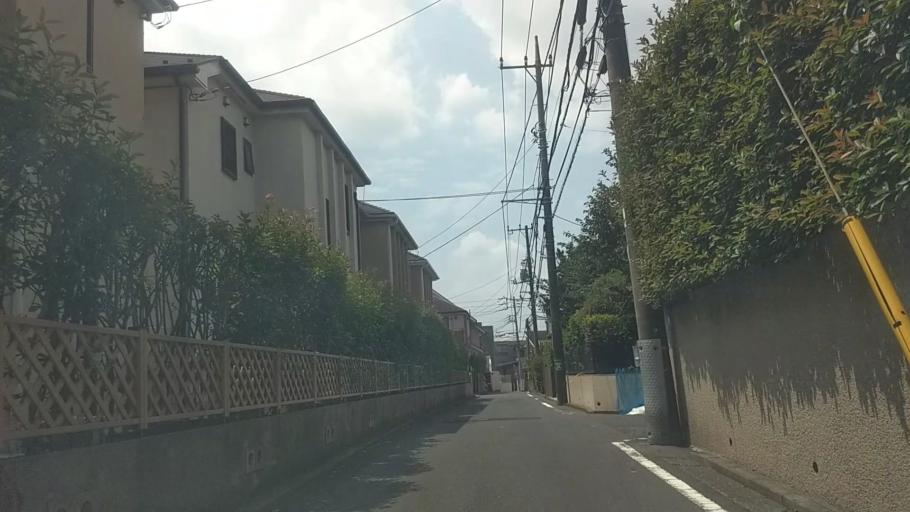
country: JP
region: Kanagawa
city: Yokohama
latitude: 35.5064
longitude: 139.6277
